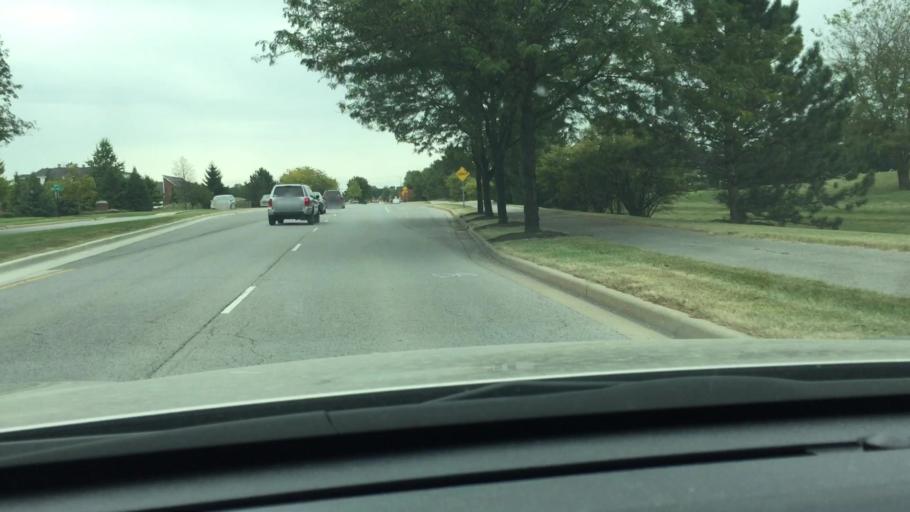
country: US
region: Indiana
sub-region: Hamilton County
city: Carmel
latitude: 39.9753
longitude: -86.0706
